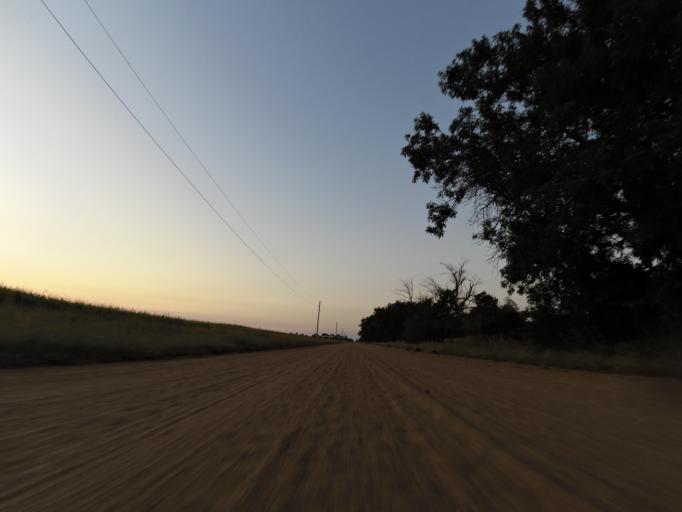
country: US
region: Kansas
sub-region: Reno County
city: South Hutchinson
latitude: 37.9577
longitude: -98.0319
